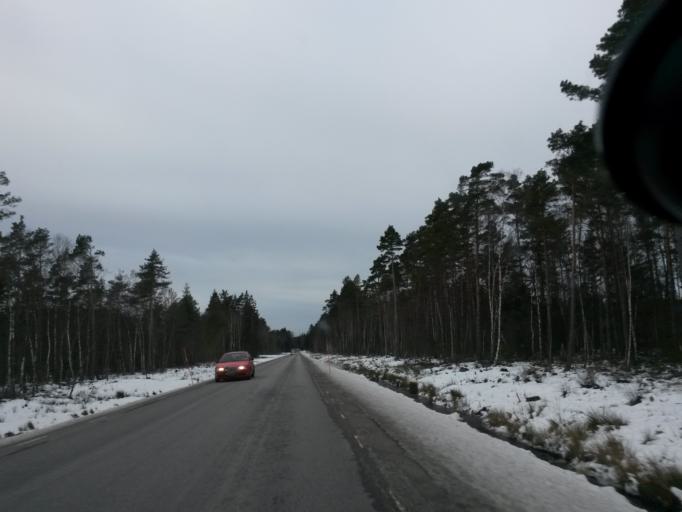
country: SE
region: Vaestra Goetaland
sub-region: Vargarda Kommun
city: Jonstorp
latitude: 57.9430
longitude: 12.6748
